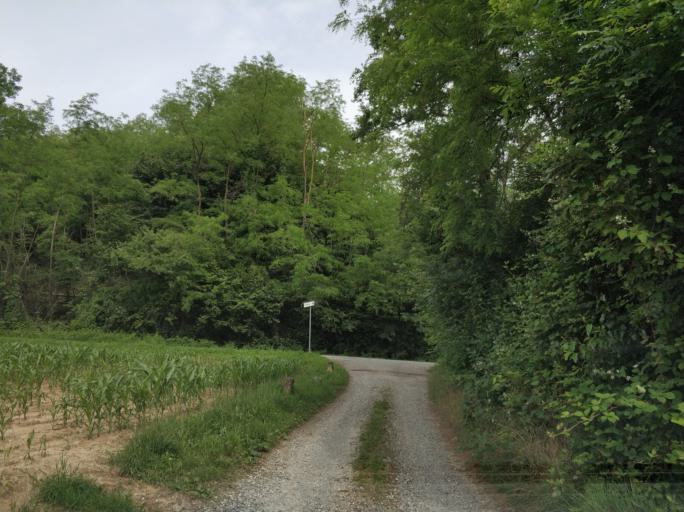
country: IT
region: Piedmont
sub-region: Provincia di Torino
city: Levone
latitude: 45.3209
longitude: 7.6213
